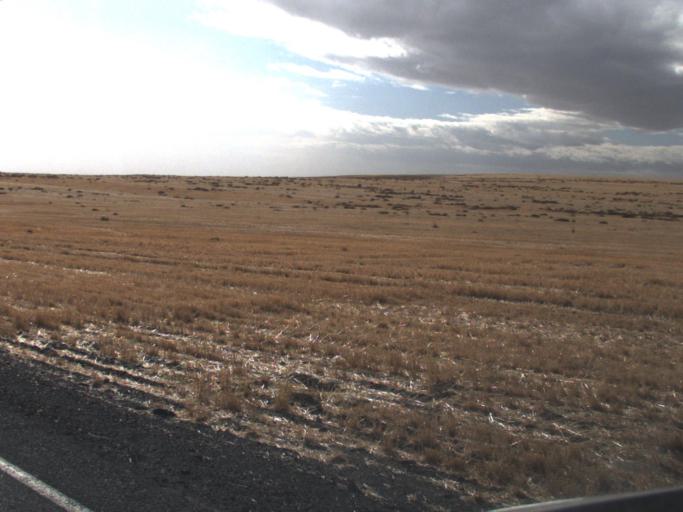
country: US
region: Washington
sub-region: Okanogan County
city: Coulee Dam
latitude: 47.4777
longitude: -118.7848
